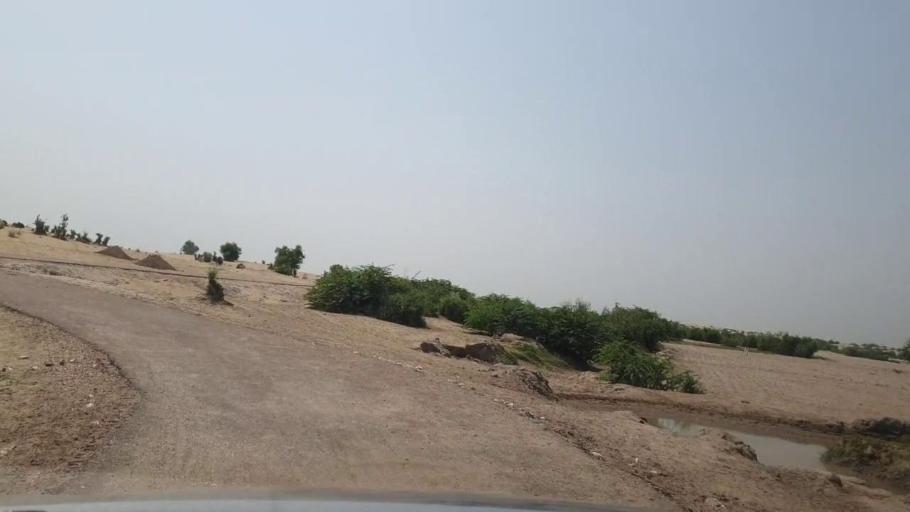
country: PK
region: Sindh
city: Pano Aqil
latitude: 27.6084
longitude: 69.1464
